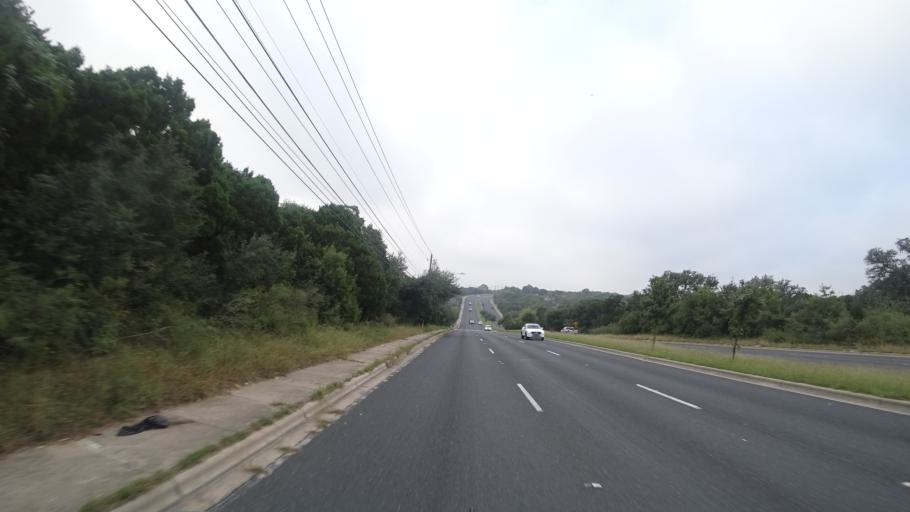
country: US
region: Texas
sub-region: Travis County
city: Wells Branch
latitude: 30.3668
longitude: -97.6687
